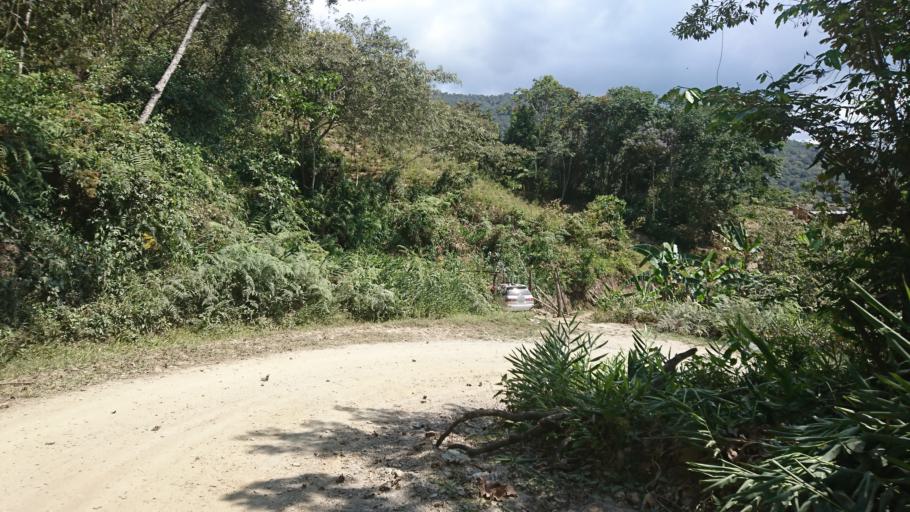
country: BO
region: La Paz
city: Coroico
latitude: -16.0596
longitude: -67.8030
